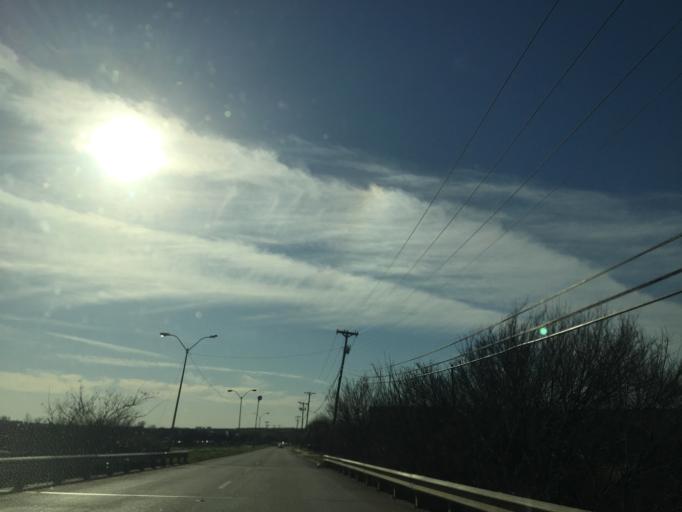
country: US
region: Texas
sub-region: Tarrant County
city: Euless
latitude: 32.8308
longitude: -97.0249
